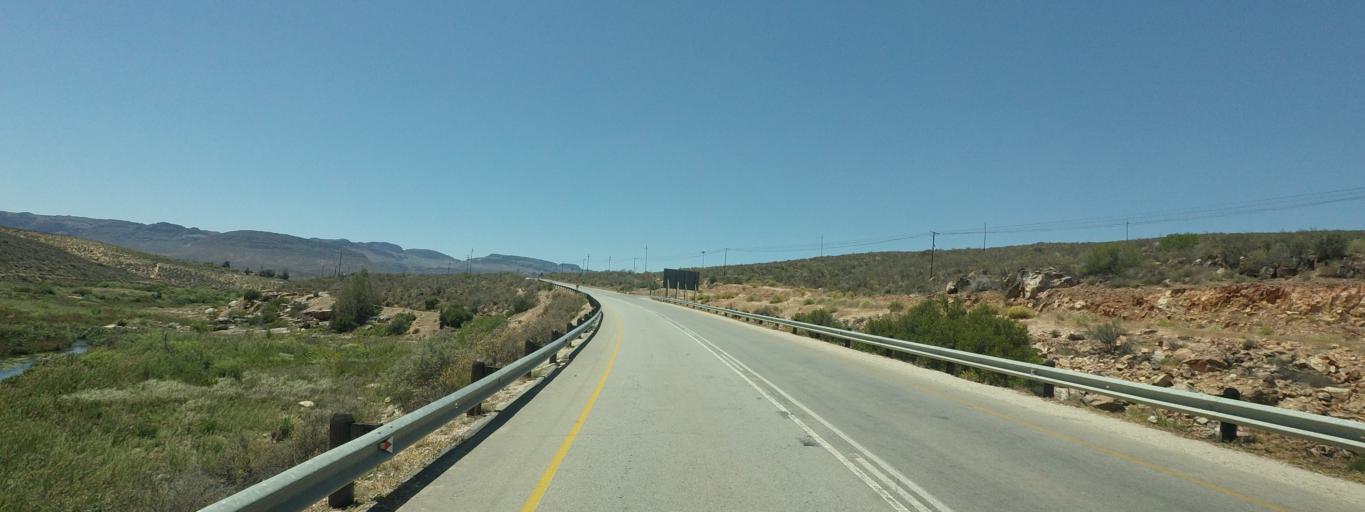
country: ZA
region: Western Cape
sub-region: West Coast District Municipality
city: Clanwilliam
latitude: -32.1727
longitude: 18.8714
